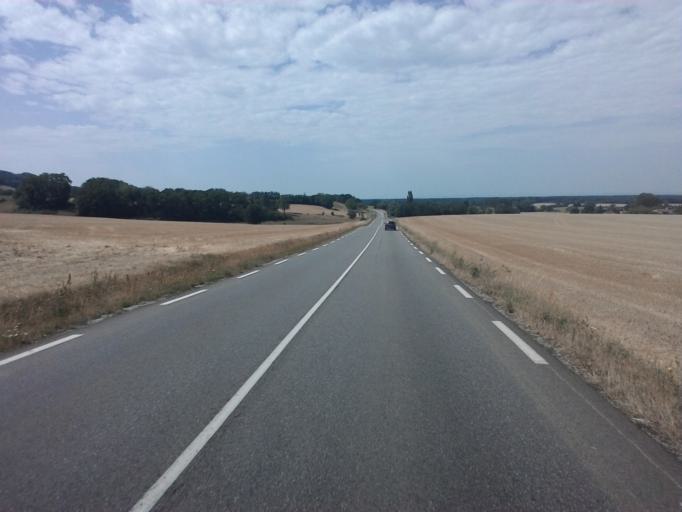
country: FR
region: Franche-Comte
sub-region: Departement du Jura
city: Cousance
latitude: 46.5686
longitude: 5.4216
